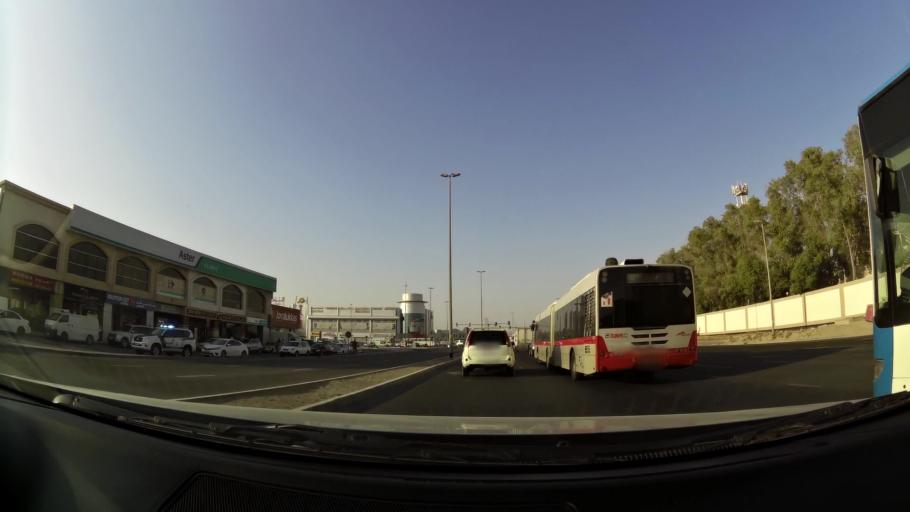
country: AE
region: Dubai
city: Dubai
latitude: 25.1469
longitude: 55.2461
